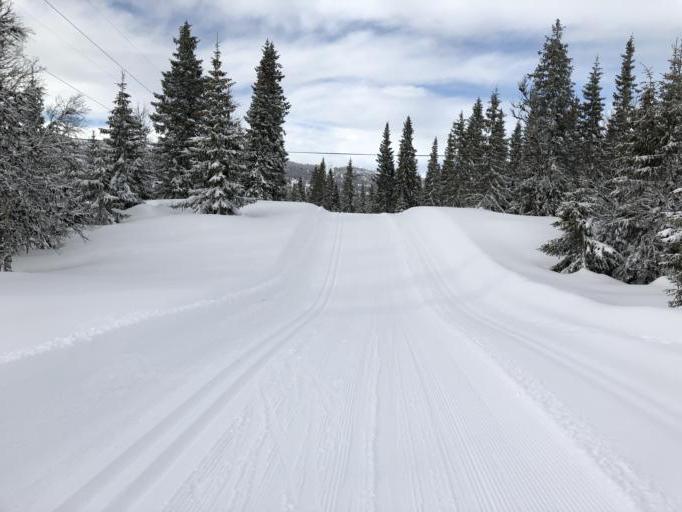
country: NO
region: Oppland
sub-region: Gausdal
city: Segalstad bru
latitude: 61.3233
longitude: 10.0798
